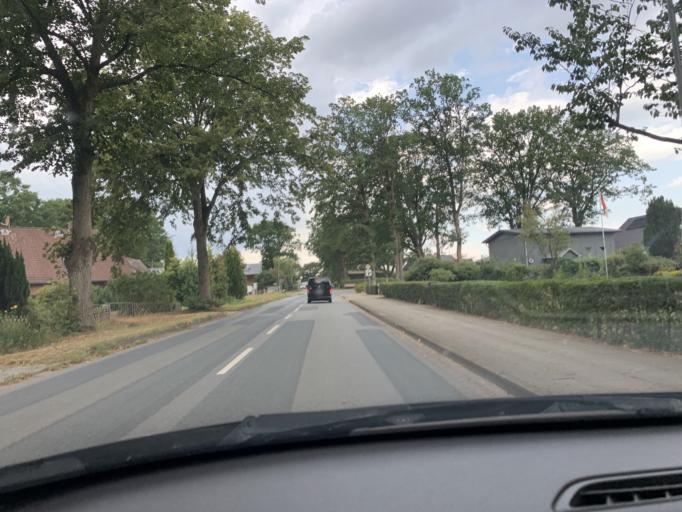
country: DE
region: Lower Saxony
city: Heidenau
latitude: 53.3171
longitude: 9.6445
